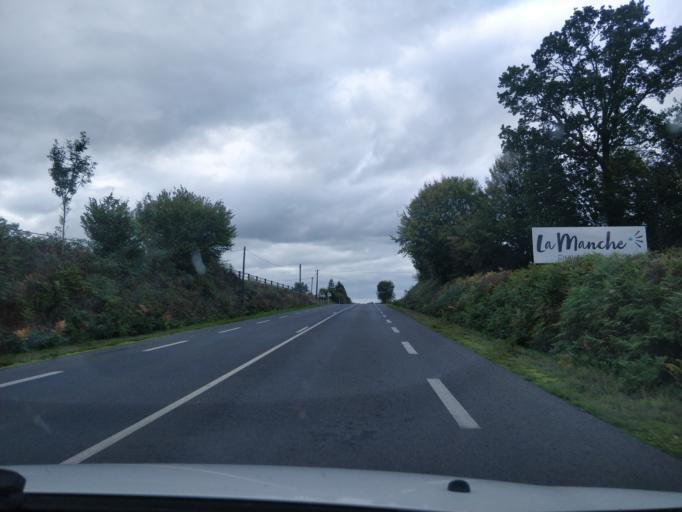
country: FR
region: Lower Normandy
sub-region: Departement de la Manche
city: Villedieu-les-Poeles
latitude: 48.8315
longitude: -1.1711
